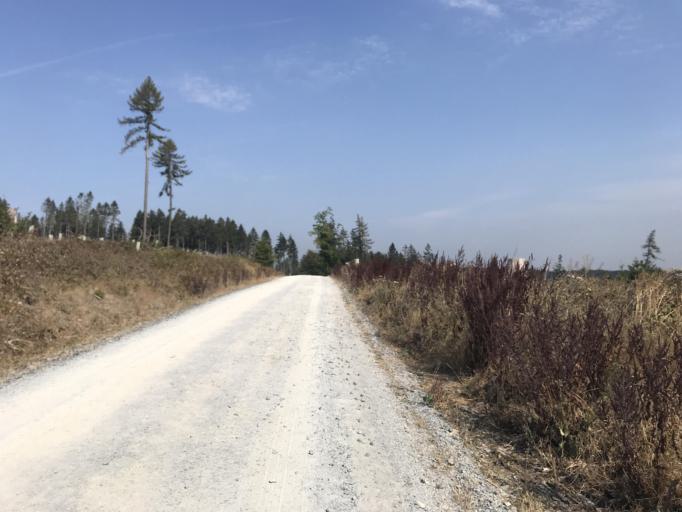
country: DE
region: Rheinland-Pfalz
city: Oestrich-Winkel
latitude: 50.0528
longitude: 8.0072
